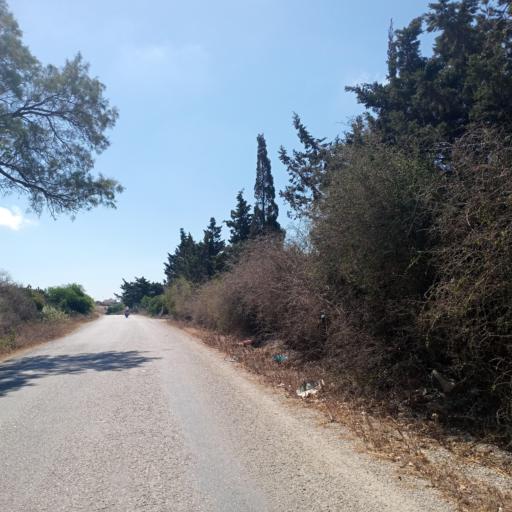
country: TN
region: Nabul
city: Qulaybiyah
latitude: 36.8608
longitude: 11.0428
